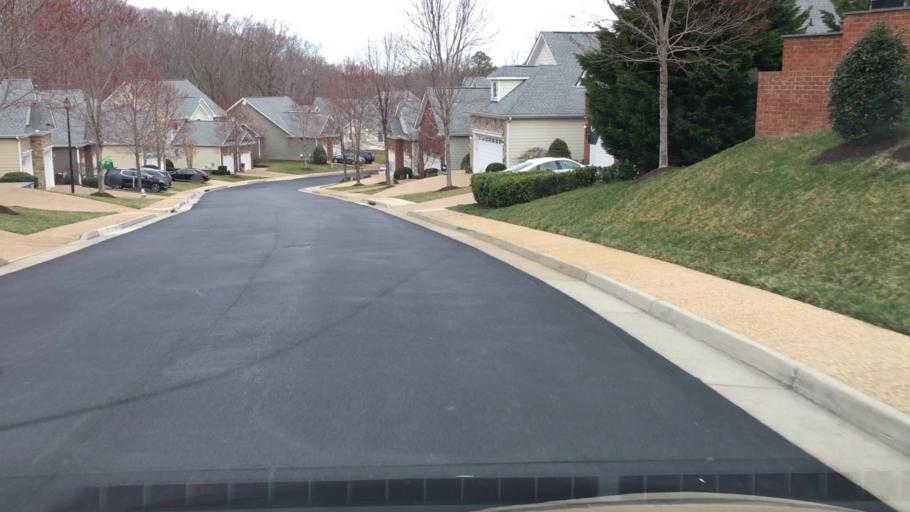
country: US
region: Virginia
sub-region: Chesterfield County
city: Bon Air
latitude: 37.5419
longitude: -77.5571
